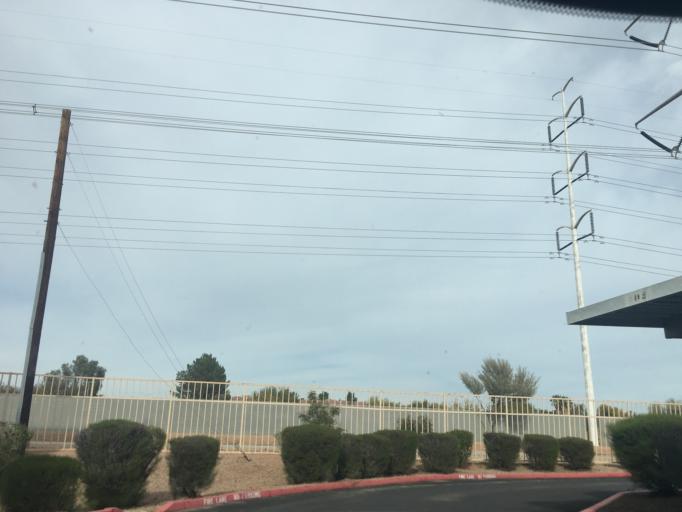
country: US
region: Arizona
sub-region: Maricopa County
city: Gilbert
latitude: 33.3569
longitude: -111.7882
